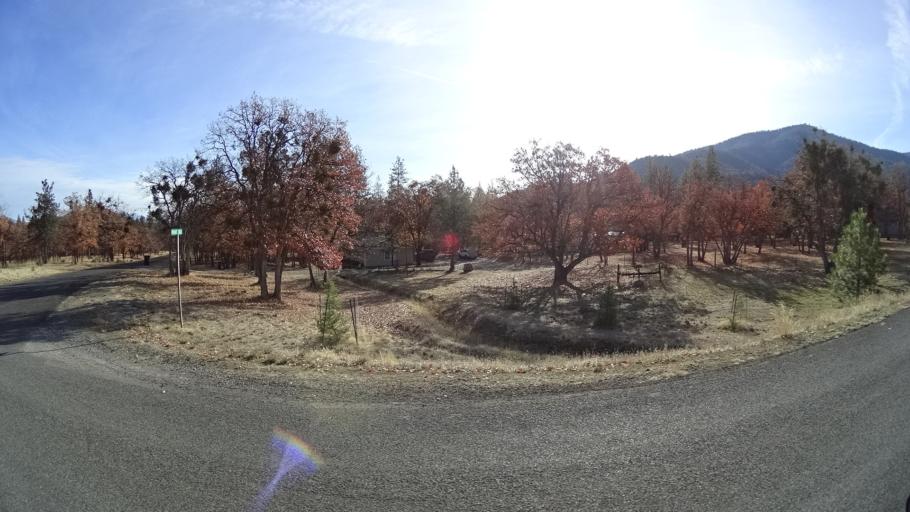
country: US
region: California
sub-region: Siskiyou County
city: Yreka
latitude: 41.6617
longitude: -122.6237
